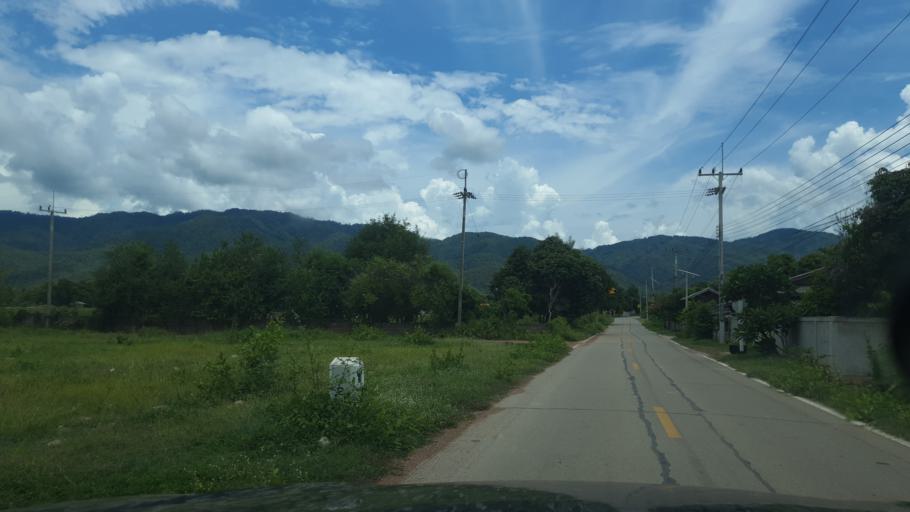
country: TH
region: Lampang
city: Sop Prap
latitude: 17.9111
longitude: 99.4131
